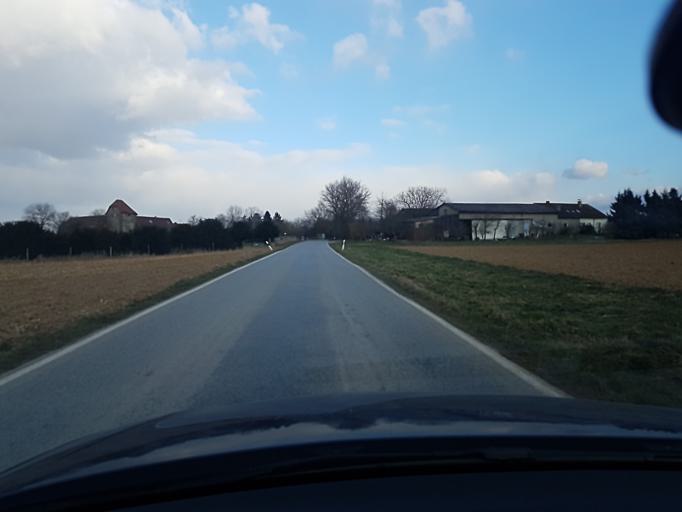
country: DE
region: Baden-Wuerttemberg
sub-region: Regierungsbezirk Stuttgart
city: Talheim
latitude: 49.0687
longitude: 9.1940
